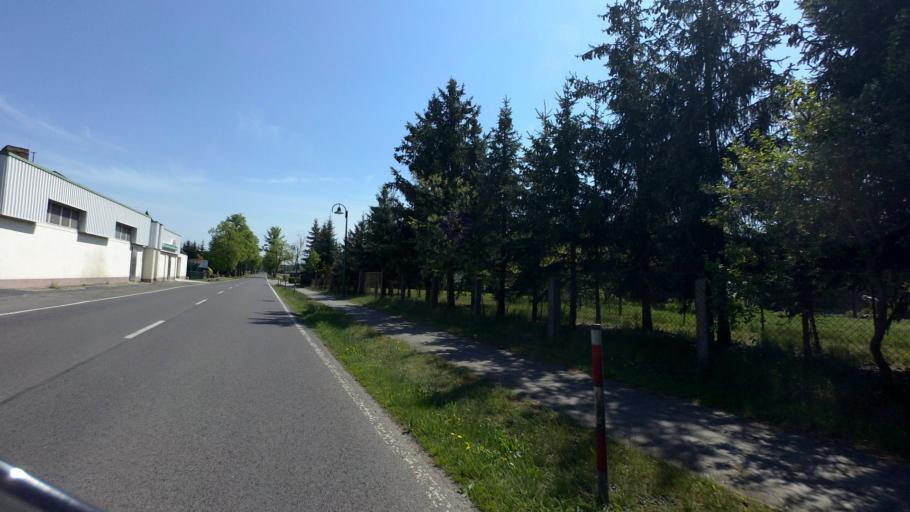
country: DE
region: Brandenburg
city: Schlepzig
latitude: 52.0586
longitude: 13.9589
